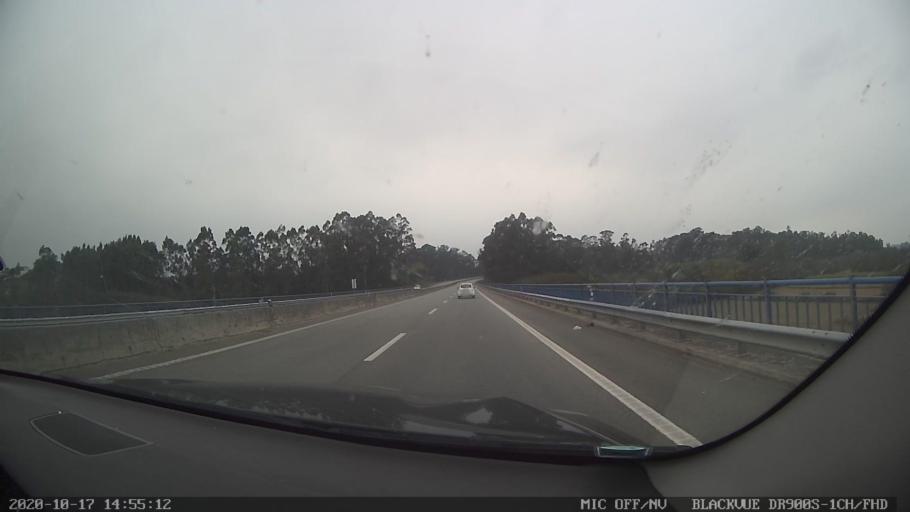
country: PT
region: Braga
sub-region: Esposende
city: Apulia
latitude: 41.4926
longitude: -8.7086
